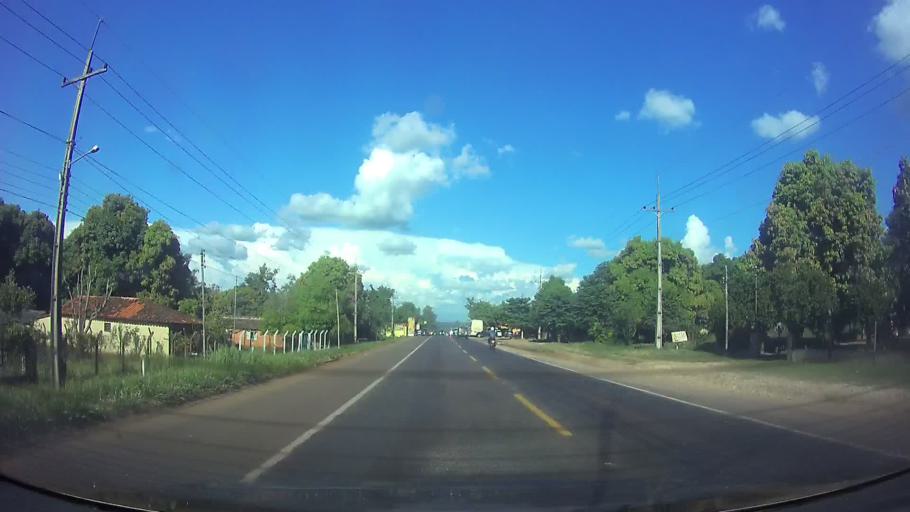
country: PY
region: Cordillera
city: Eusebio Ayala
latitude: -25.3818
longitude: -57.0027
